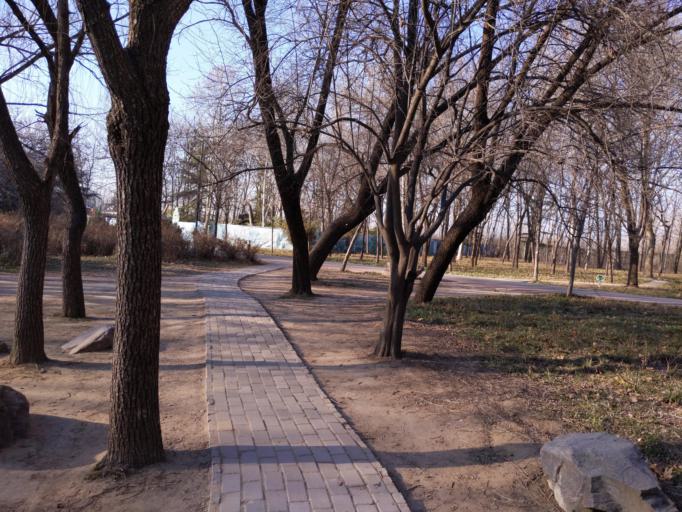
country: CN
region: Henan Sheng
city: Puyang
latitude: 35.7790
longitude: 114.9612
